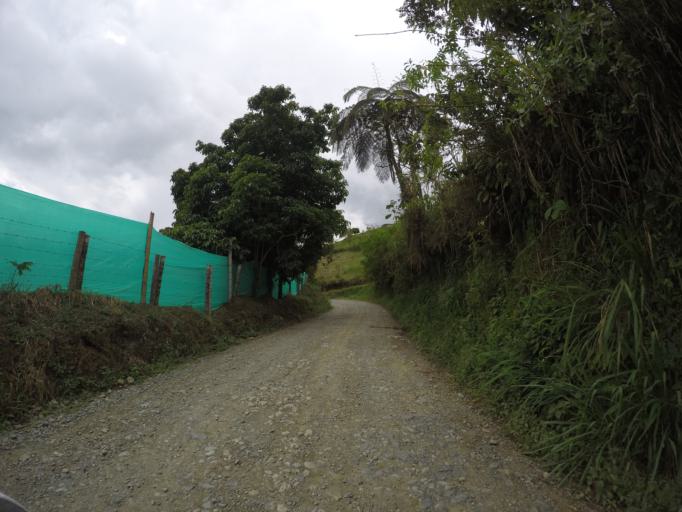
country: CO
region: Quindio
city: Filandia
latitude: 4.6512
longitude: -75.6738
